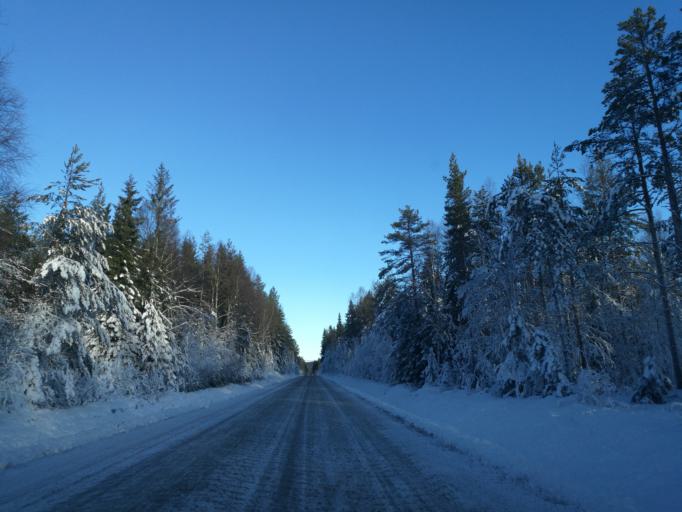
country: NO
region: Hedmark
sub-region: Grue
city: Kirkenaer
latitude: 60.4744
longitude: 12.5541
